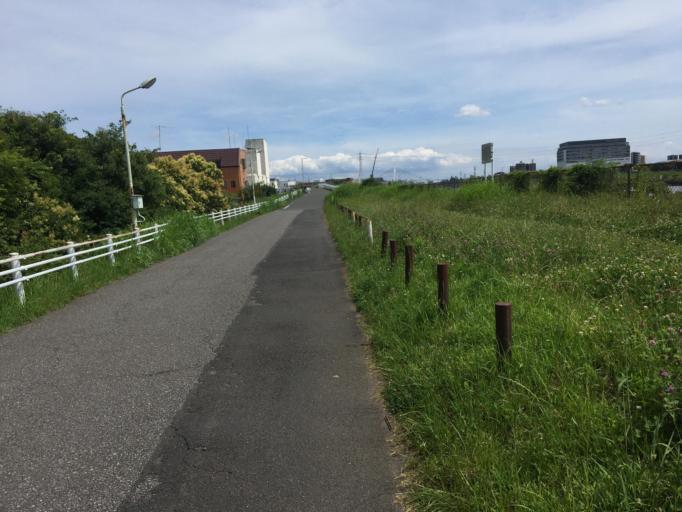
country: JP
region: Chiba
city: Matsudo
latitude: 35.7581
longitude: 139.8582
